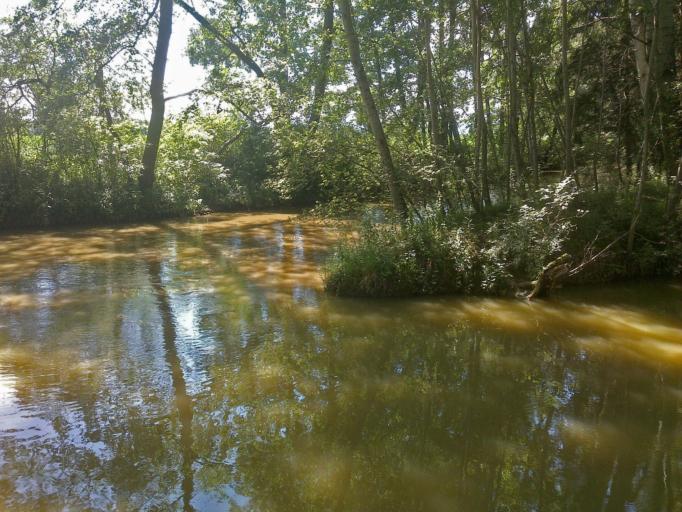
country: AT
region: Styria
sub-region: Politischer Bezirk Leibnitz
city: Sankt Georgen an der Stiefing
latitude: 46.8504
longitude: 15.5662
